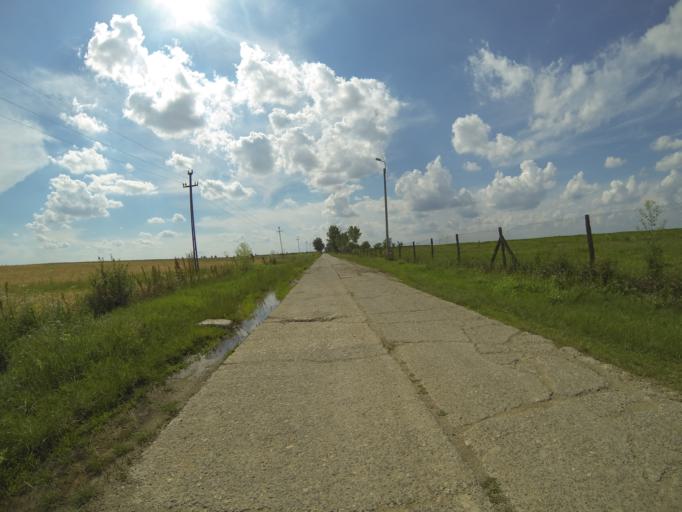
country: RO
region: Dolj
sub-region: Comuna Segarcea
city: Segarcea
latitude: 44.1080
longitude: 23.7351
